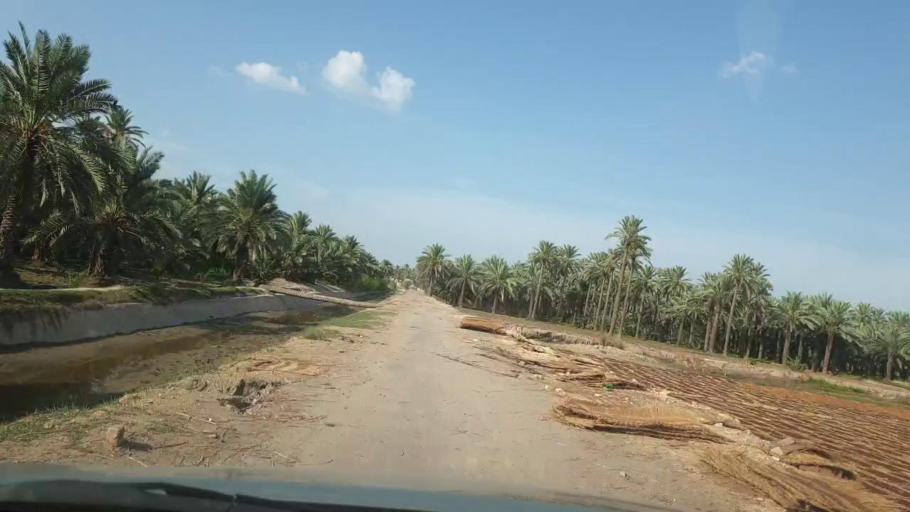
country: PK
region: Sindh
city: Sukkur
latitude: 27.6510
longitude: 68.8276
